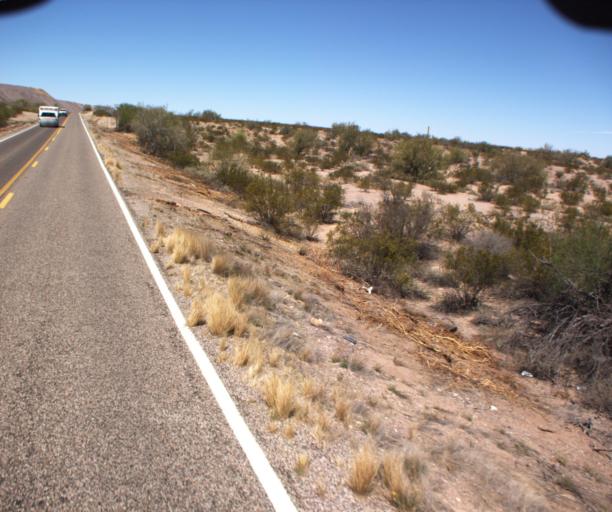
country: US
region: Arizona
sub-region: Pima County
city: Ajo
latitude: 32.3503
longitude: -112.8174
